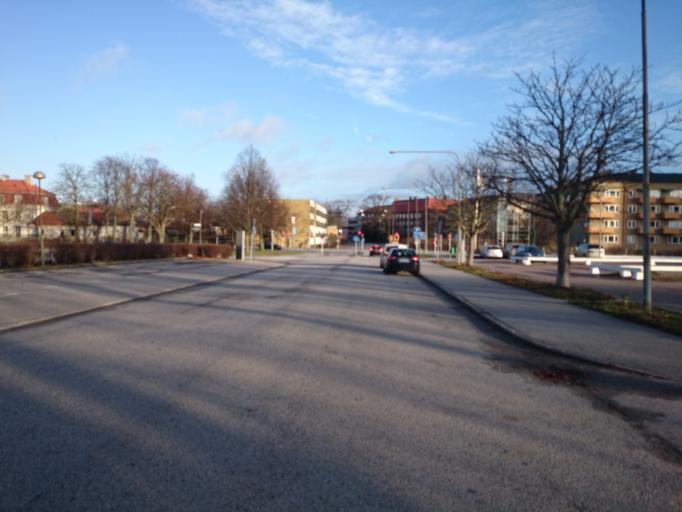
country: SE
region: Skane
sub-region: Malmo
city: Malmoe
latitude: 55.5845
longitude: 13.0029
